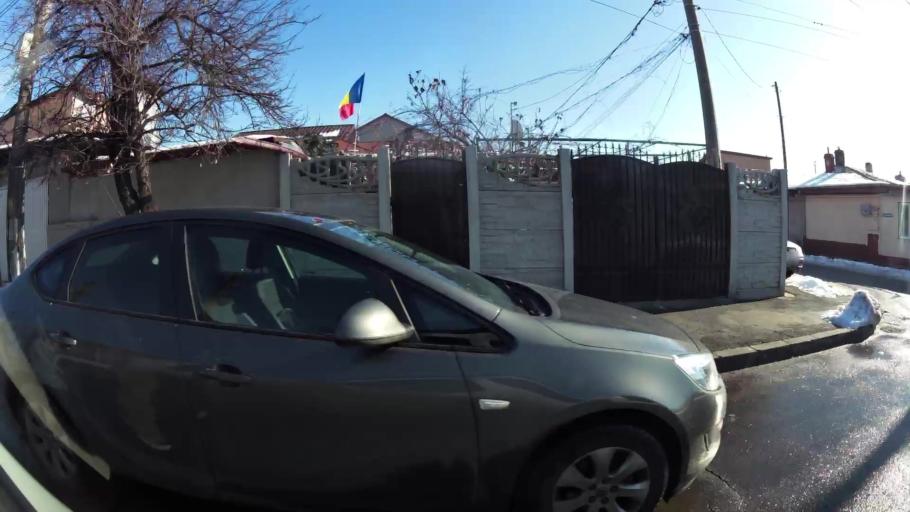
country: RO
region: Ilfov
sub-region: Comuna Magurele
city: Magurele
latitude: 44.3919
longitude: 26.0540
